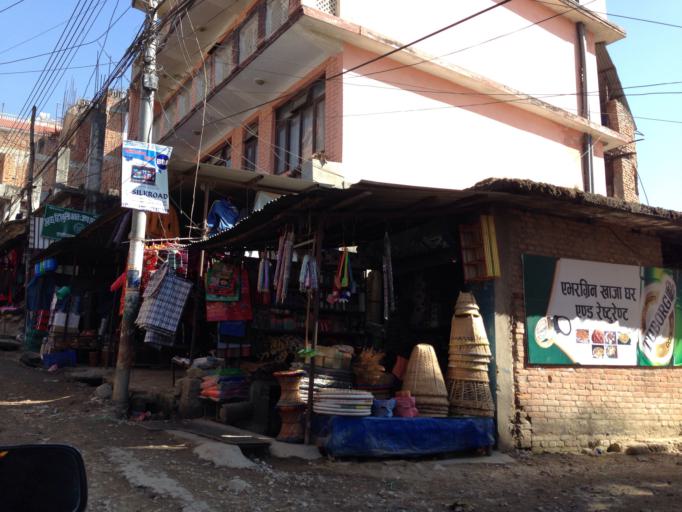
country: NP
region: Central Region
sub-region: Bagmati Zone
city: Kathmandu
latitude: 27.7772
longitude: 85.3625
